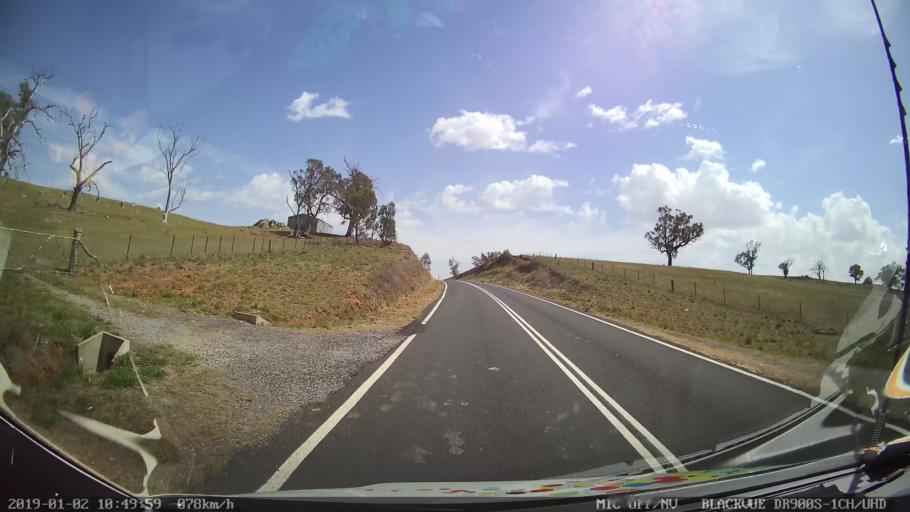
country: AU
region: New South Wales
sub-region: Cootamundra
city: Cootamundra
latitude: -34.7179
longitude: 148.2771
